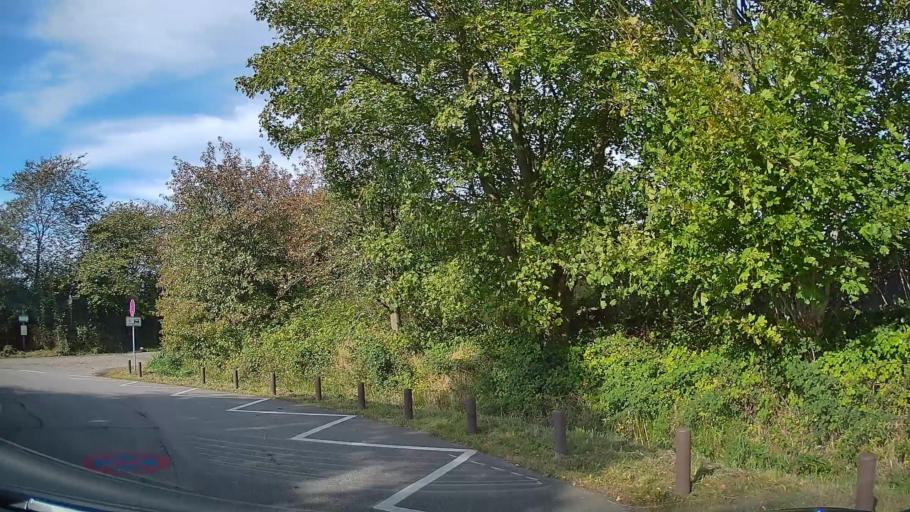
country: DK
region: South Denmark
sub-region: Sonderborg Kommune
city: Grasten
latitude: 54.8718
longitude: 9.6004
